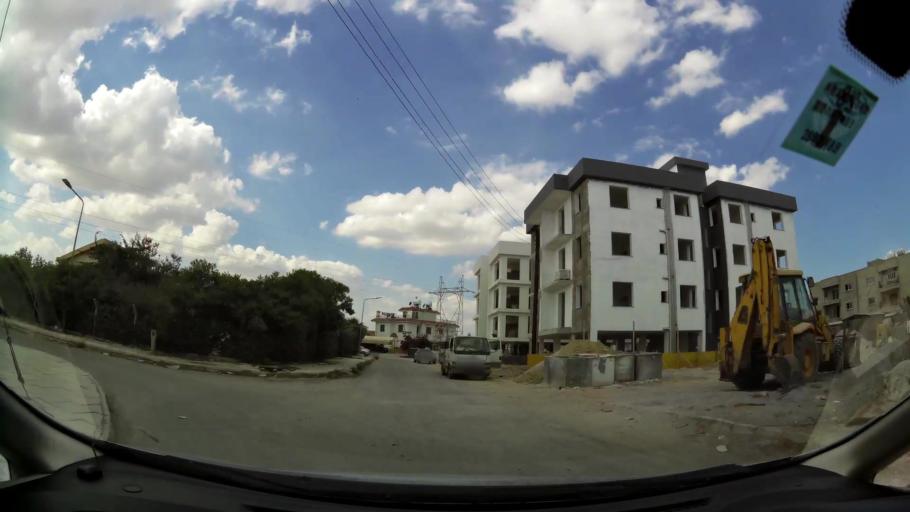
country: CY
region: Lefkosia
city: Nicosia
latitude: 35.2090
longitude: 33.3749
